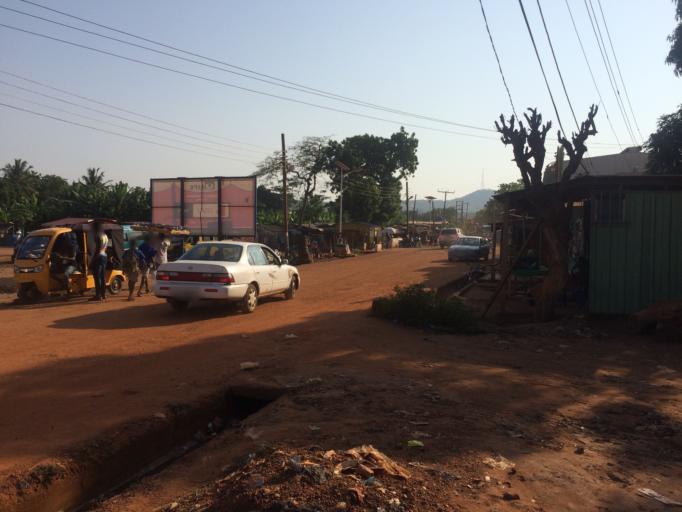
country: GH
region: Greater Accra
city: Medina Estates
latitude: 5.7307
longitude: -0.2045
